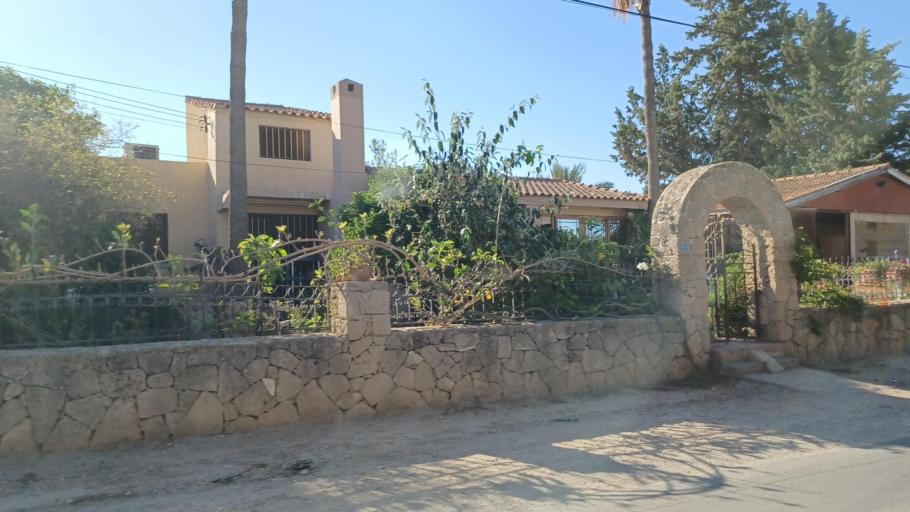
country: CY
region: Larnaka
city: Pergamos
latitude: 35.0358
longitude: 33.7065
